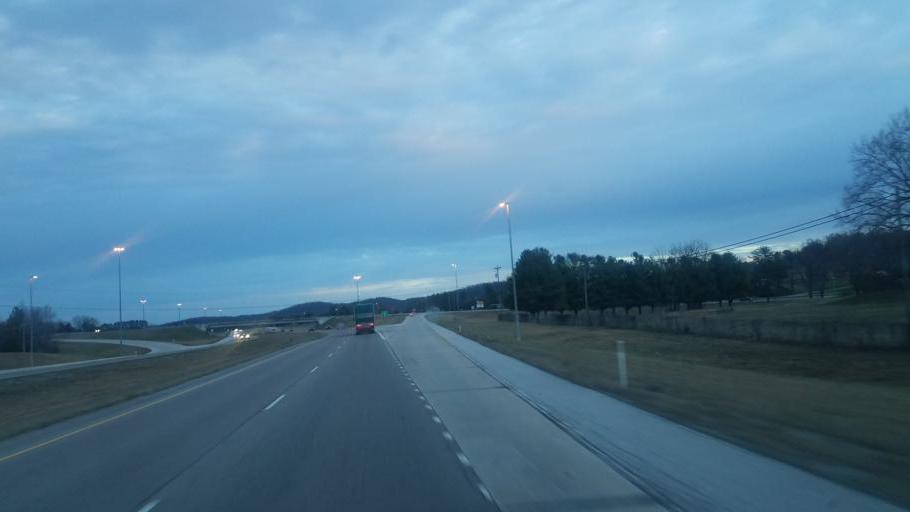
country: US
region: Tennessee
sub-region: White County
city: Sparta
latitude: 35.9618
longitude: -85.4857
